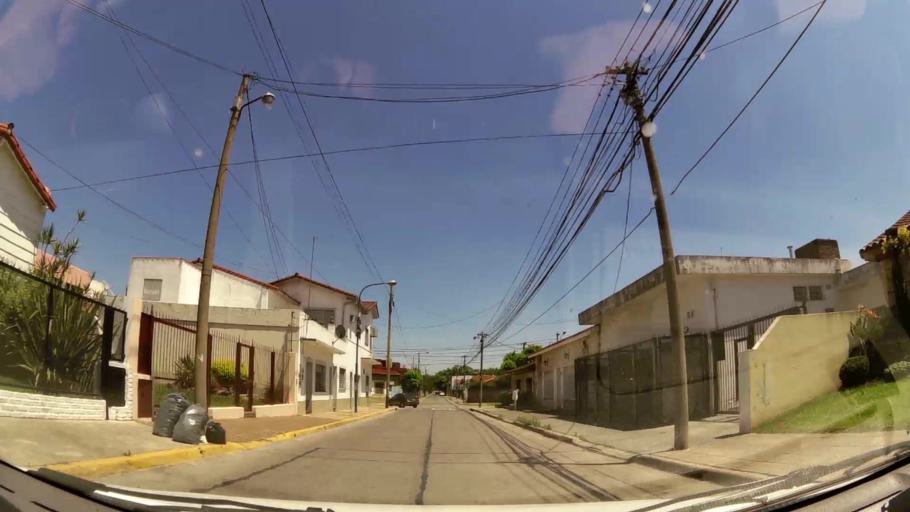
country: AR
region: Buenos Aires
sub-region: Partido de Merlo
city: Merlo
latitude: -34.6651
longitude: -58.7049
